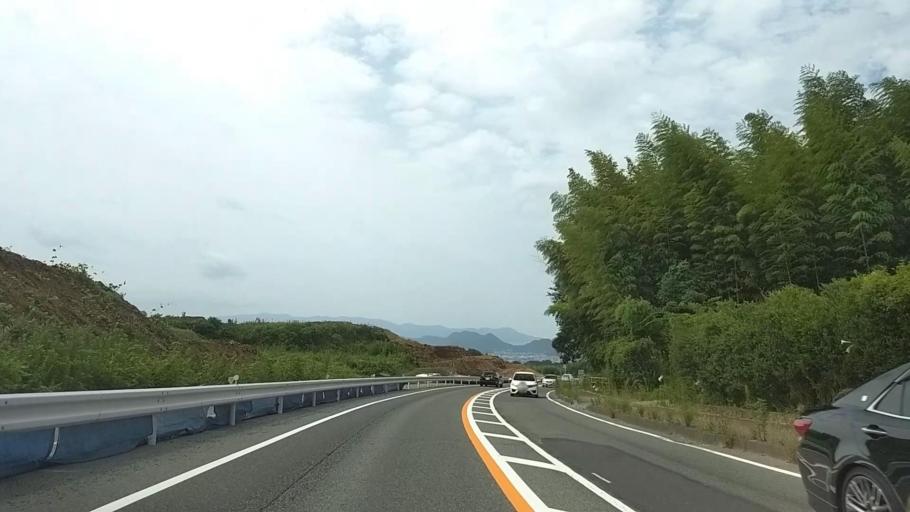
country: JP
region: Shizuoka
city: Mishima
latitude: 35.1397
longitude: 138.9721
